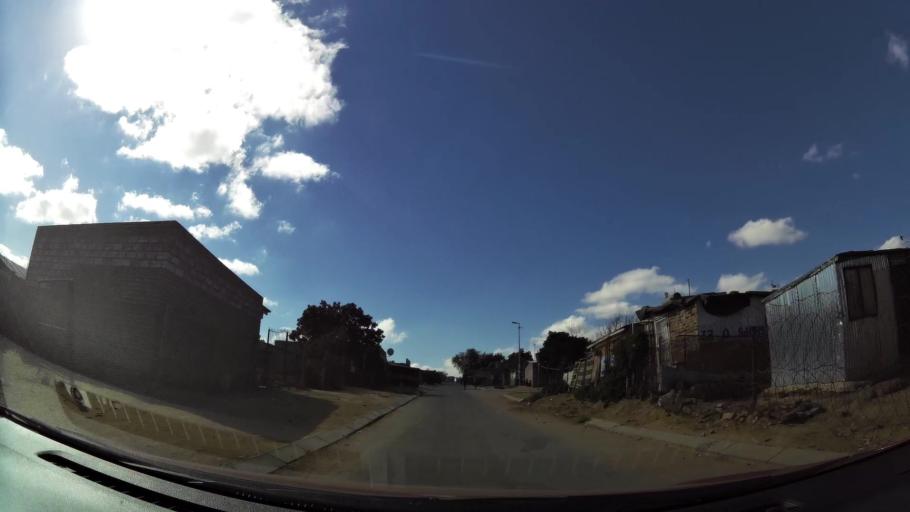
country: ZA
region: Gauteng
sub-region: City of Johannesburg Metropolitan Municipality
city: Midrand
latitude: -26.0299
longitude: 28.1655
